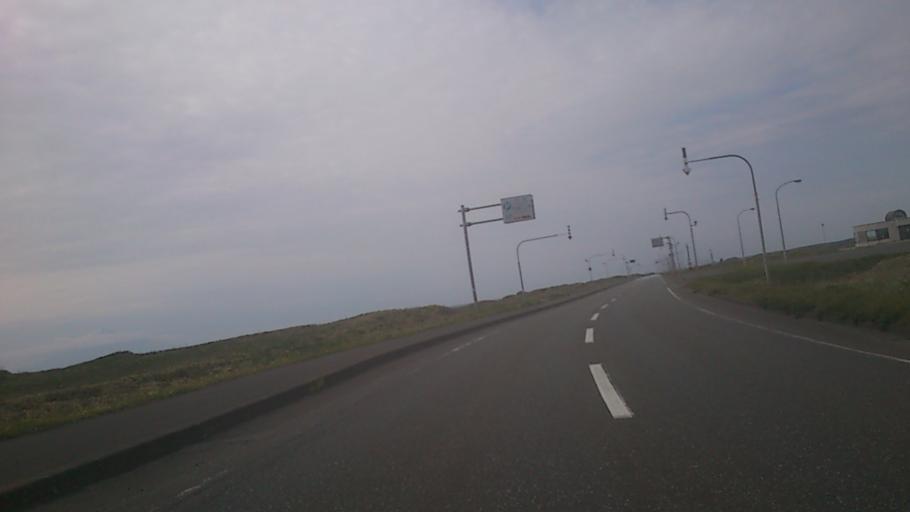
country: JP
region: Hokkaido
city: Makubetsu
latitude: 44.9239
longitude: 141.7226
